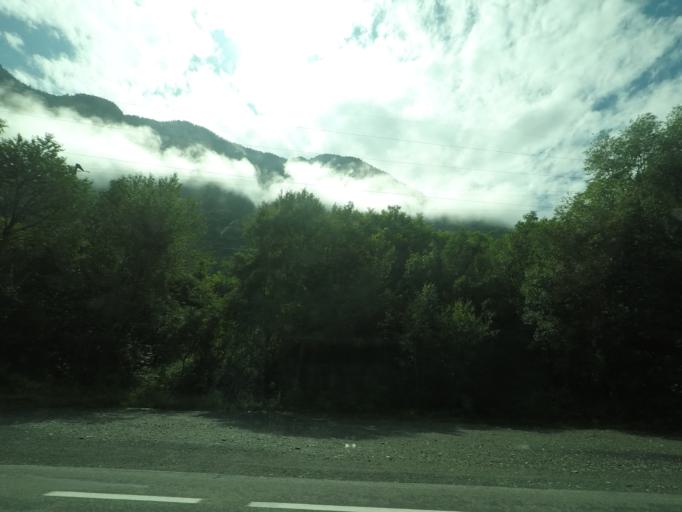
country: IT
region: Aosta Valley
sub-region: Valle d'Aosta
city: Antey-Saint-Andre
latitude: 45.7822
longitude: 7.5903
